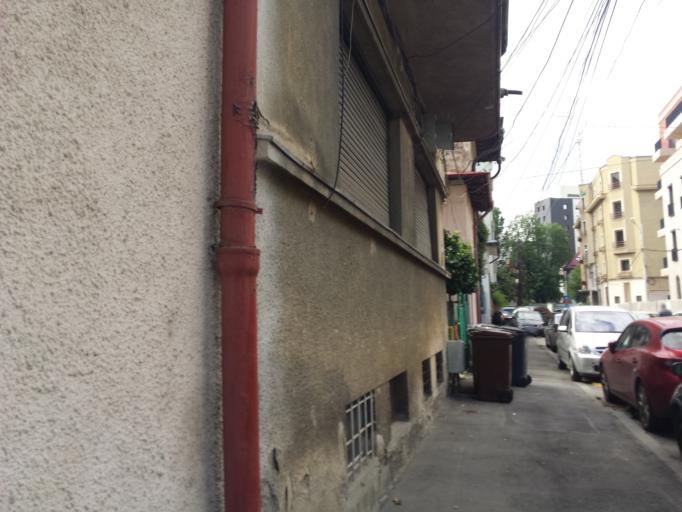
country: RO
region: Bucuresti
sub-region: Municipiul Bucuresti
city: Bucuresti
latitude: 44.4546
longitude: 26.0789
